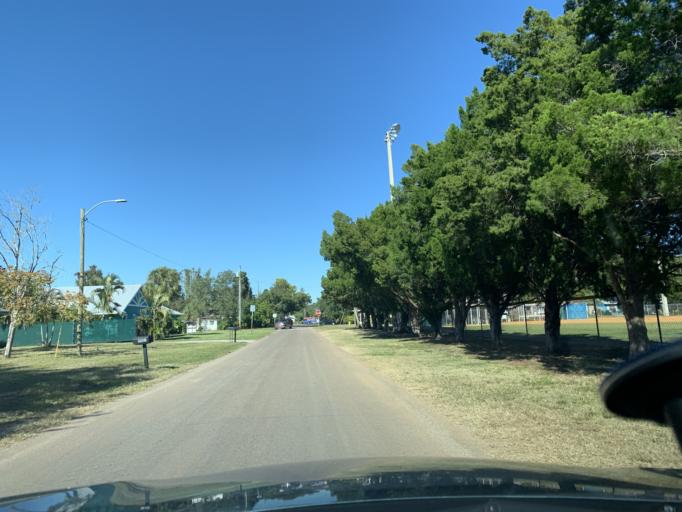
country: US
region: Florida
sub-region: Pinellas County
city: Gulfport
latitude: 27.7462
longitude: -82.7106
